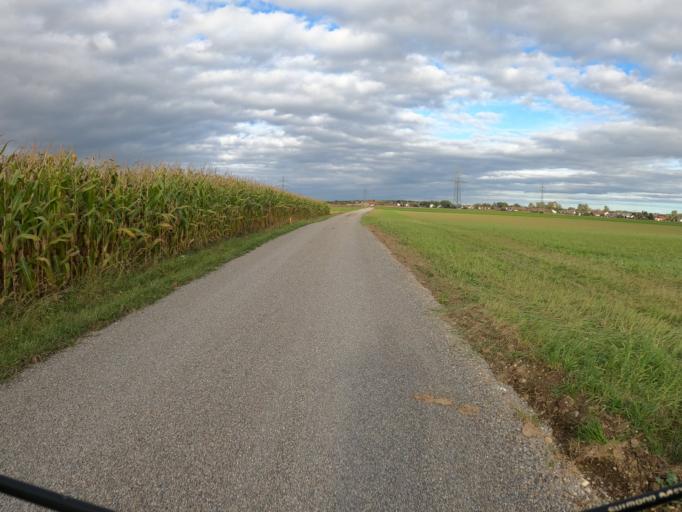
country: DE
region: Bavaria
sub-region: Swabia
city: Nersingen
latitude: 48.4112
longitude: 10.1216
